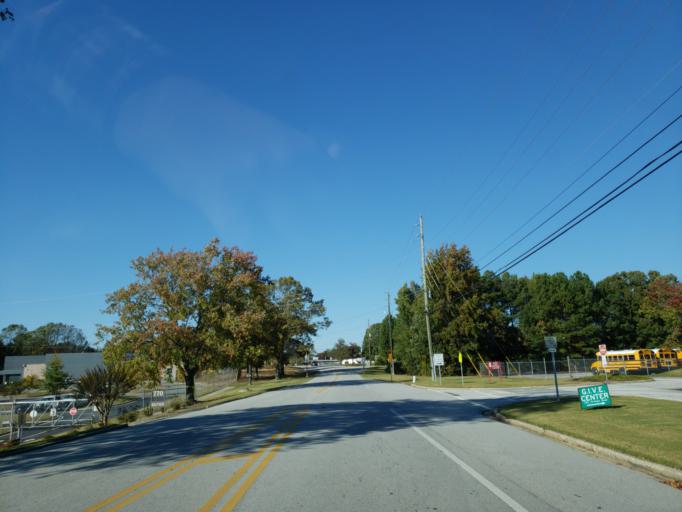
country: US
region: Georgia
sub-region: Gwinnett County
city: Lawrenceville
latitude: 33.9872
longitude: -83.9725
